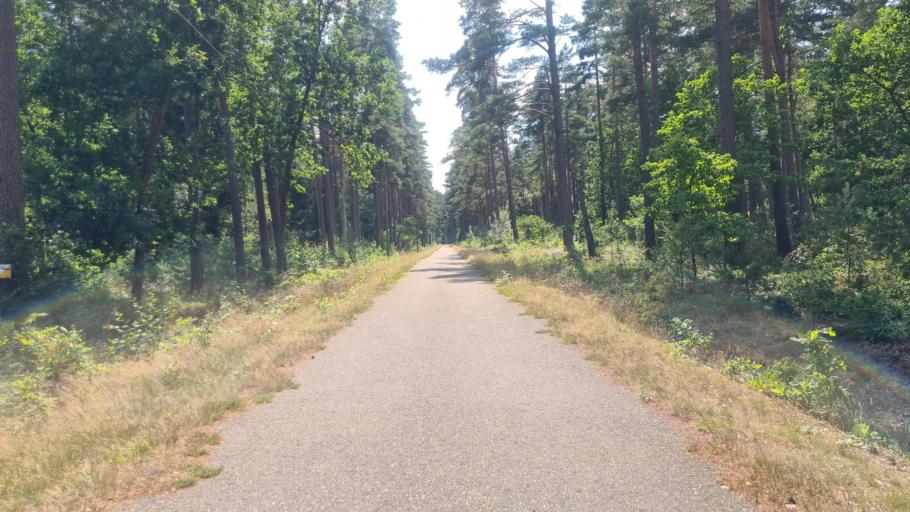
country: SE
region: Kronoberg
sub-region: Ljungby Kommun
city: Ljungby
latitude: 56.8467
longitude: 13.9648
